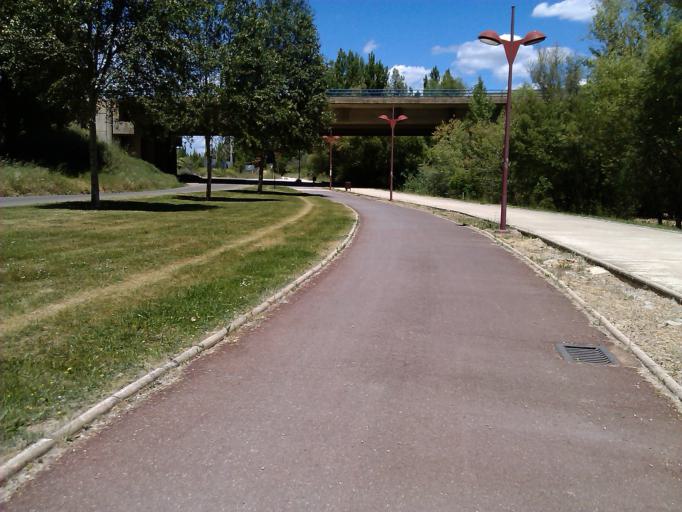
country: ES
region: Castille and Leon
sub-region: Provincia de Leon
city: Leon
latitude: 42.5855
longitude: -5.5524
